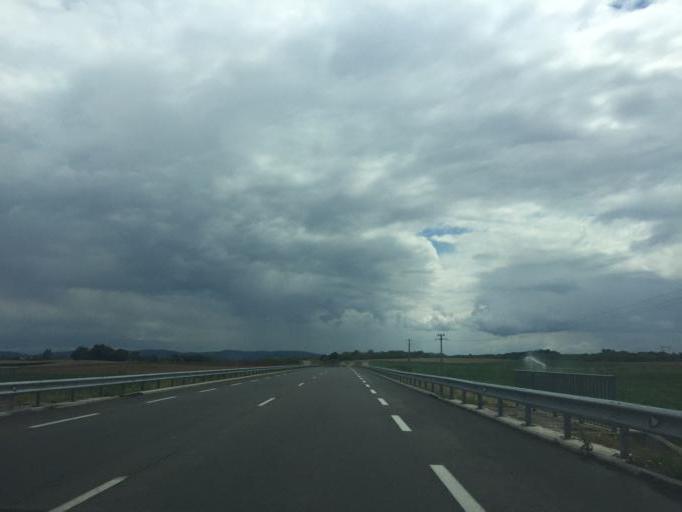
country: FR
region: Rhone-Alpes
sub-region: Departement de l'Isere
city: Janneyrias
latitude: 45.7633
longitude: 5.1235
